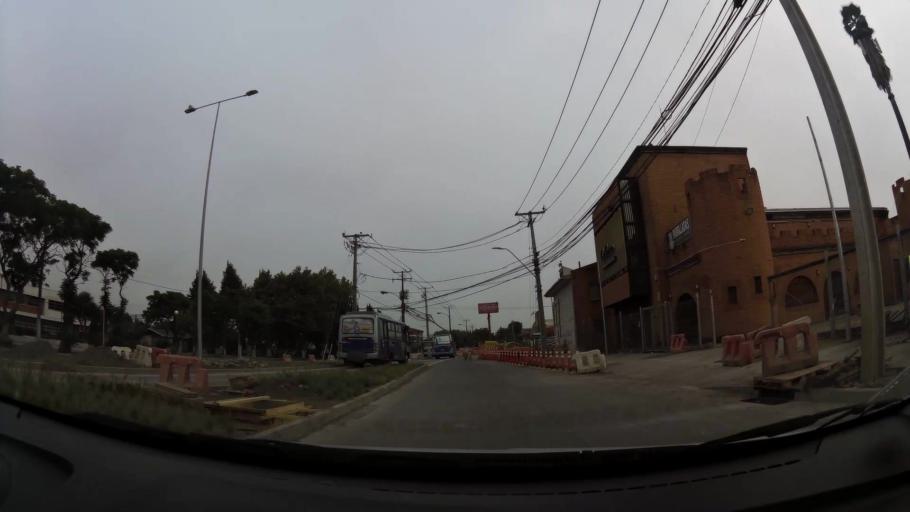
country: CL
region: Biobio
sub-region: Provincia de Concepcion
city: Concepcion
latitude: -36.7985
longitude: -73.0853
